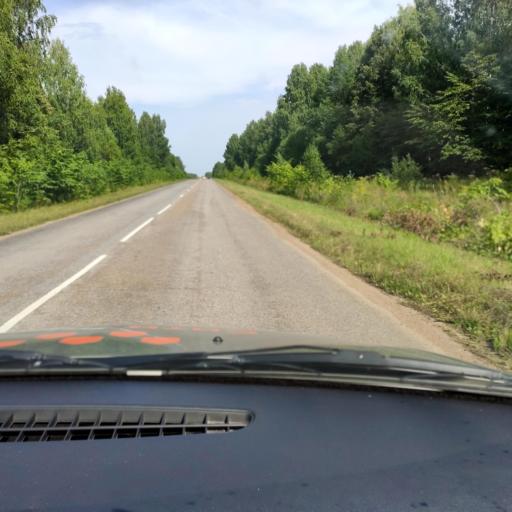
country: RU
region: Bashkortostan
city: Pavlovka
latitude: 55.3867
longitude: 56.5087
